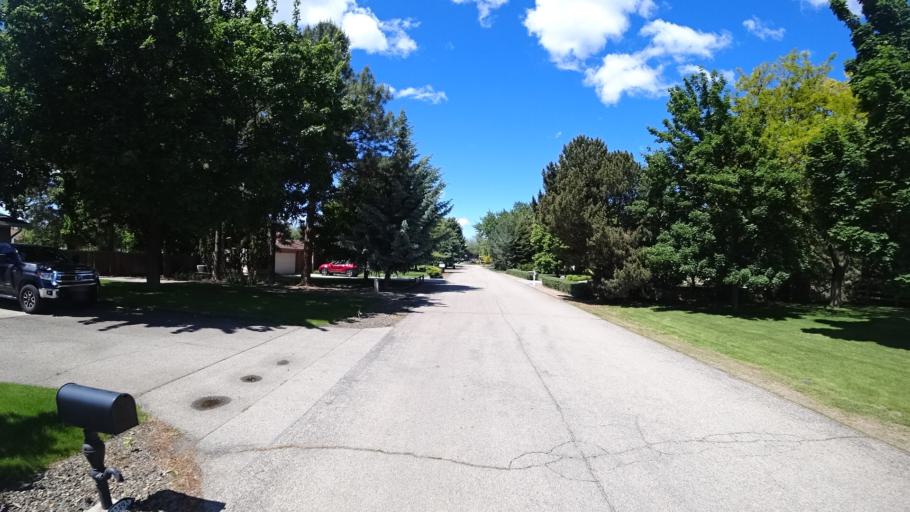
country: US
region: Idaho
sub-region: Ada County
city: Meridian
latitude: 43.6249
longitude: -116.3382
